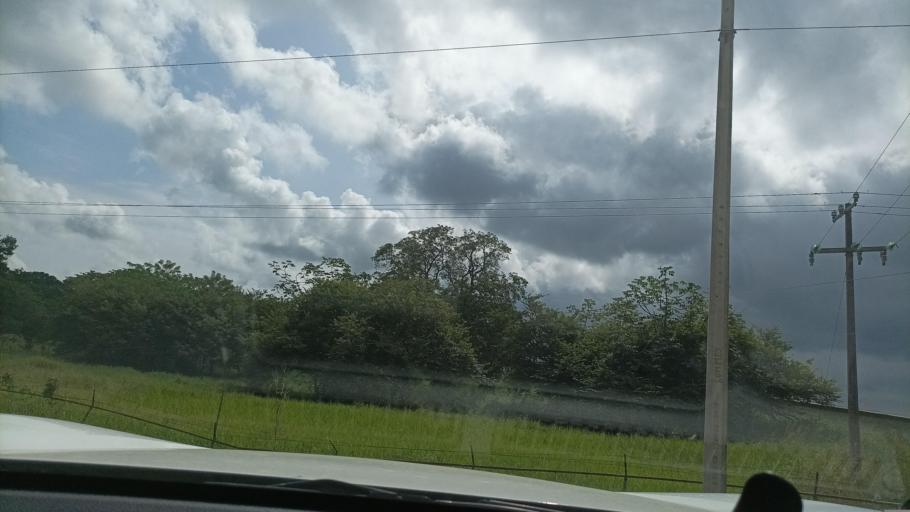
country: MX
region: Veracruz
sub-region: Chinameca
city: Chacalapa
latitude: 18.0737
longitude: -94.6943
